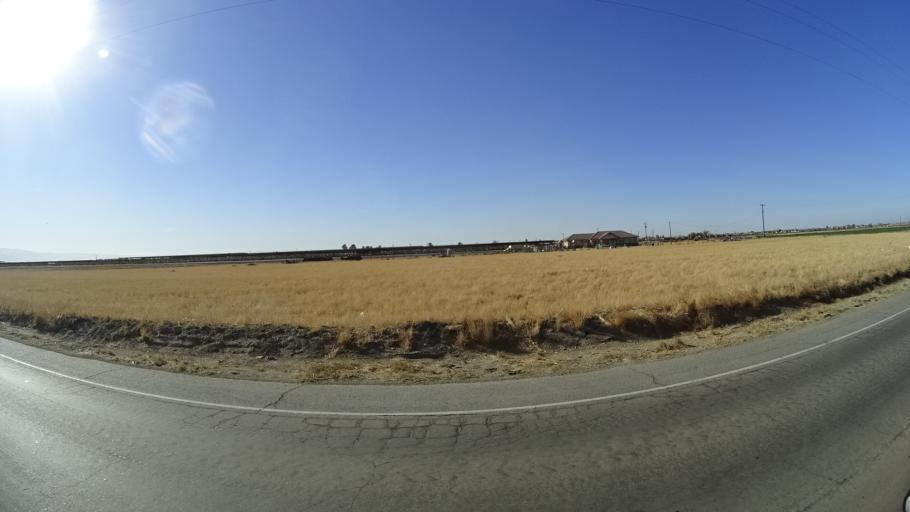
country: US
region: California
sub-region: Kern County
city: Greenfield
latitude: 35.2802
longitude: -118.9855
